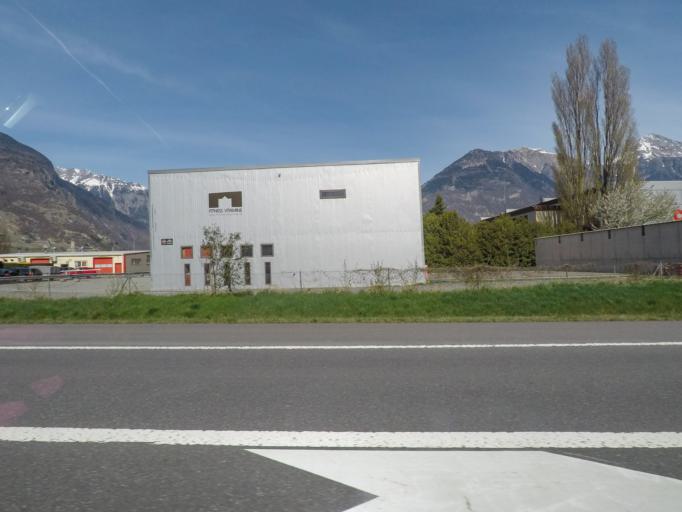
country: CH
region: Valais
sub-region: Martigny District
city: Martigny-Ville
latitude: 46.0998
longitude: 7.0883
